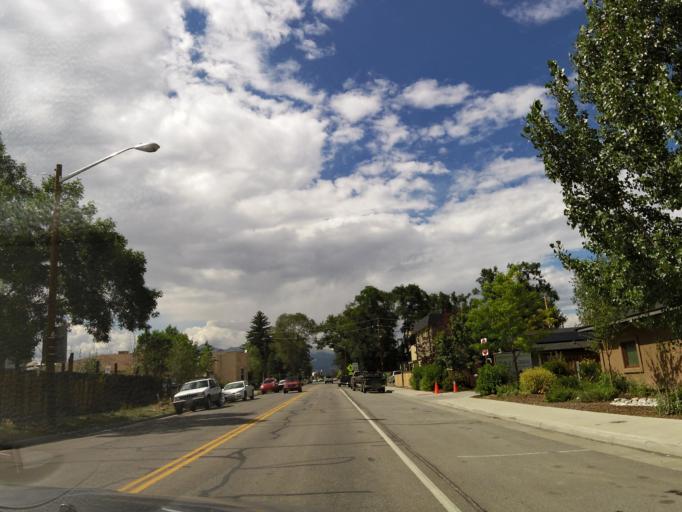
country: US
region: Colorado
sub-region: Chaffee County
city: Salida
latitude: 38.5331
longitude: -105.9866
